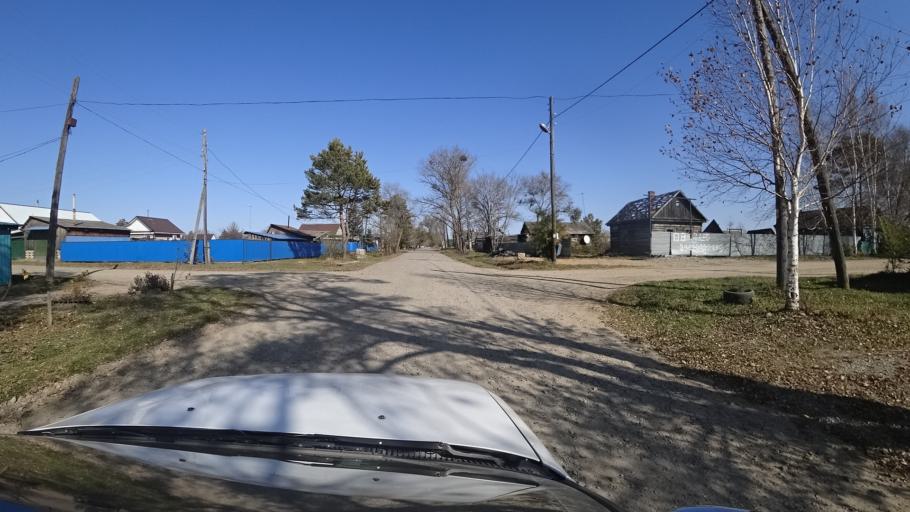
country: RU
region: Primorskiy
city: Dal'nerechensk
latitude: 45.9258
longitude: 133.7471
